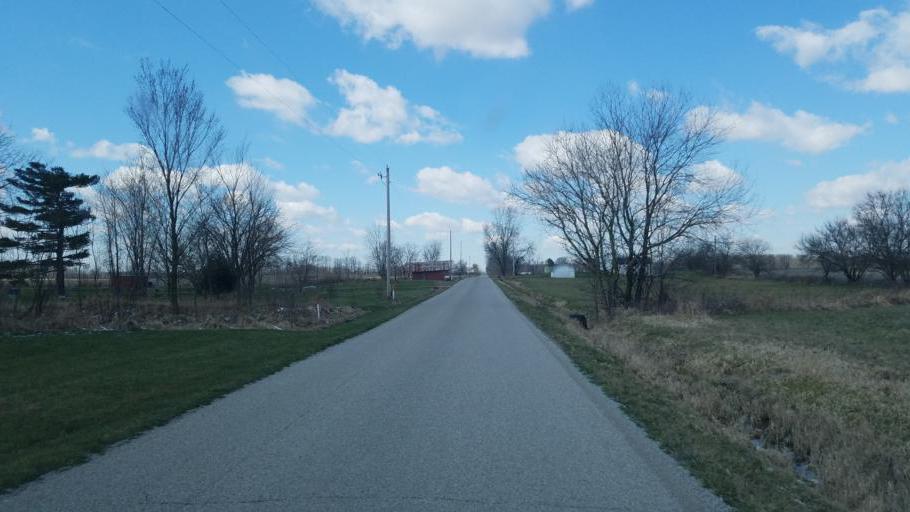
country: US
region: Ohio
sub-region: Licking County
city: Utica
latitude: 40.2667
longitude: -82.5195
